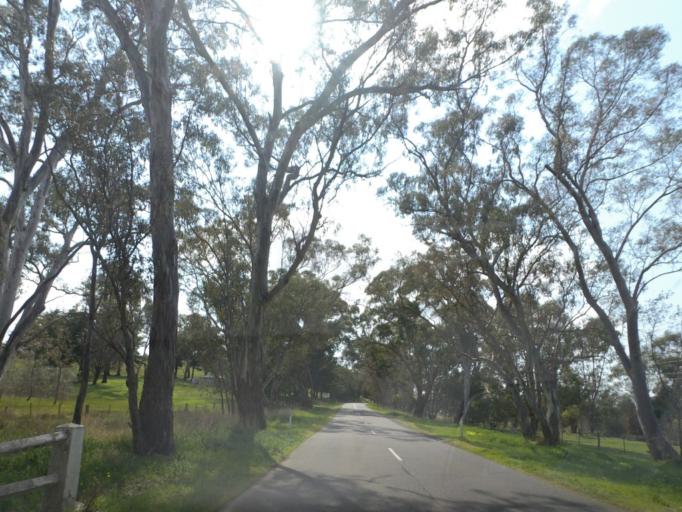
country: AU
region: Victoria
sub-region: Murrindindi
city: Kinglake West
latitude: -37.1035
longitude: 145.0964
